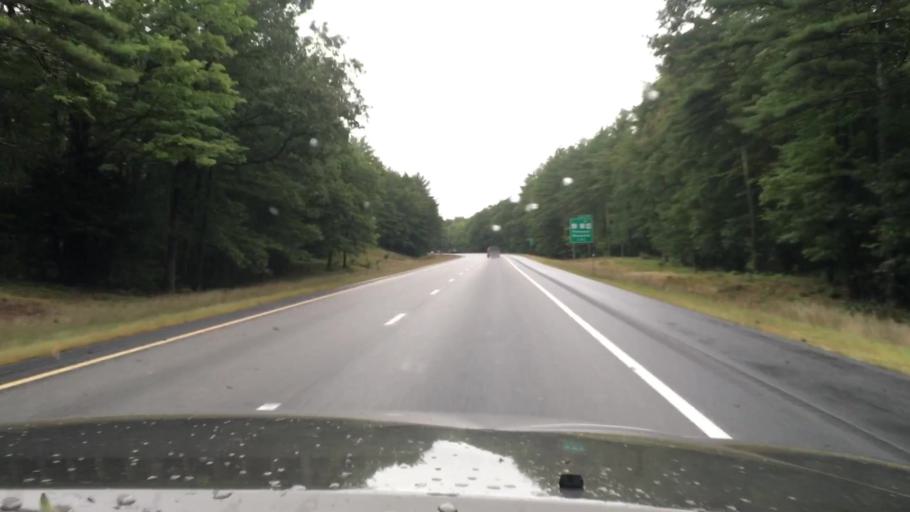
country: US
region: New Hampshire
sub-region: Merrimack County
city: Canterbury
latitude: 43.3088
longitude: -71.5859
